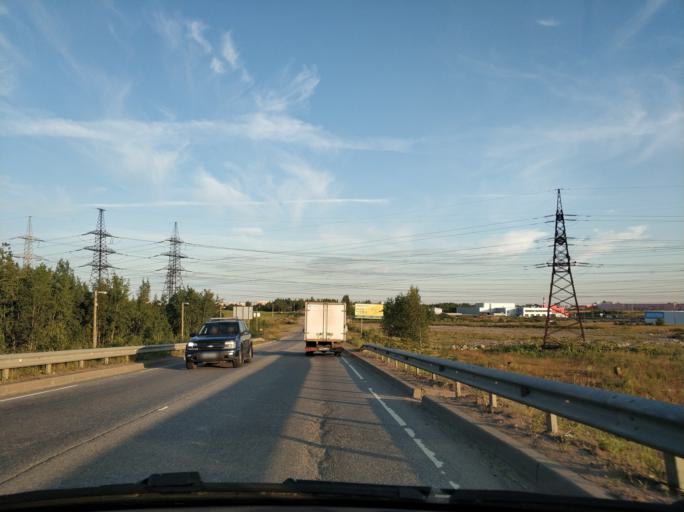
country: RU
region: Leningrad
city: Bugry
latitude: 60.1006
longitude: 30.3876
